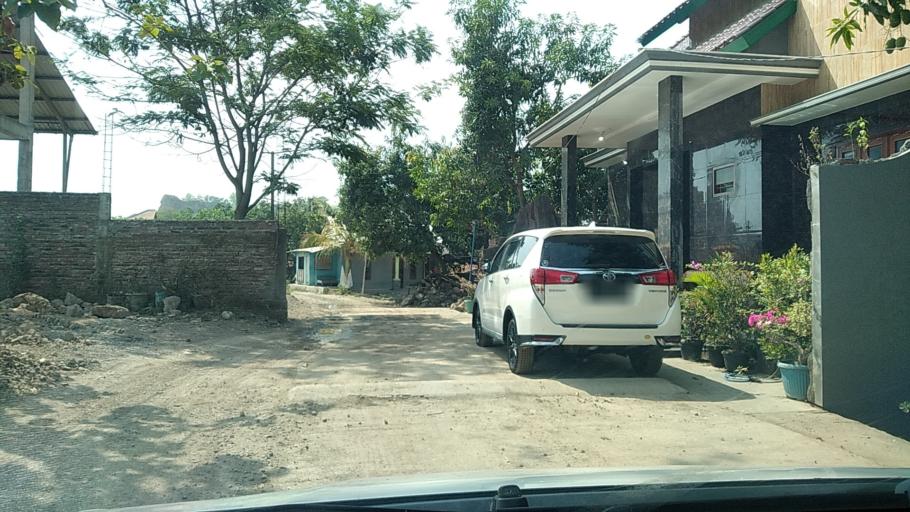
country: ID
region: Central Java
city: Mranggen
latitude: -7.0578
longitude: 110.4824
